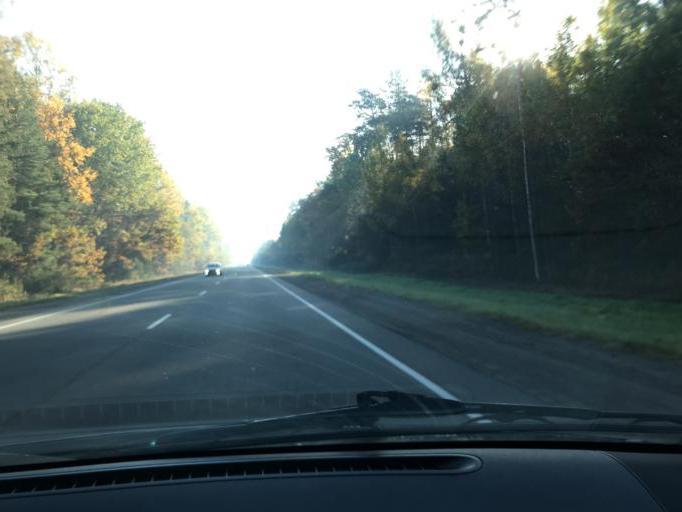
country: BY
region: Brest
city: Horad Luninyets
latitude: 52.2896
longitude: 26.7793
